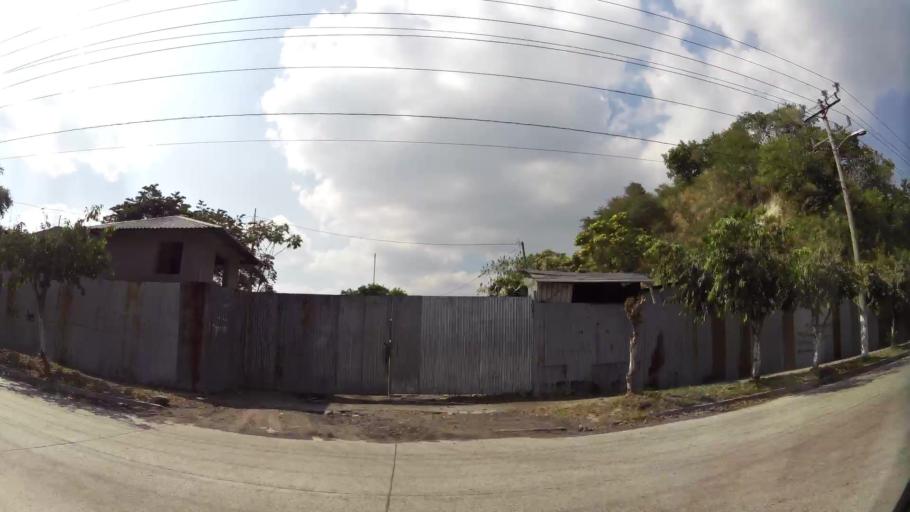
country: SV
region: San Salvador
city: Delgado
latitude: 13.7047
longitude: -89.1714
